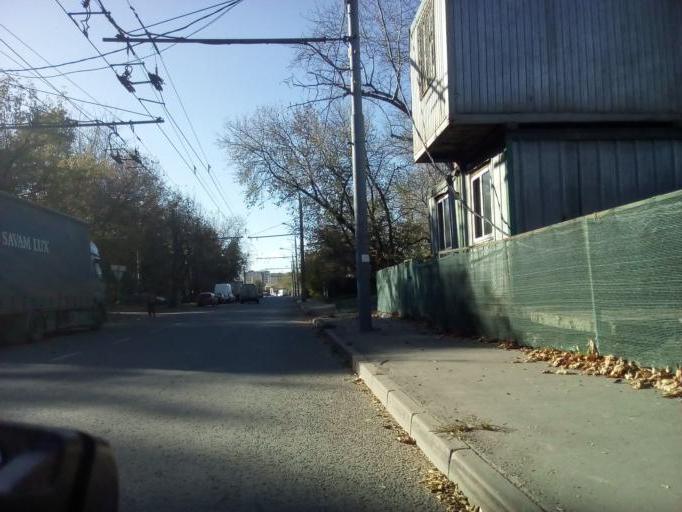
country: RU
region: Moscow
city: Likhobory
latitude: 55.8485
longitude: 37.5723
